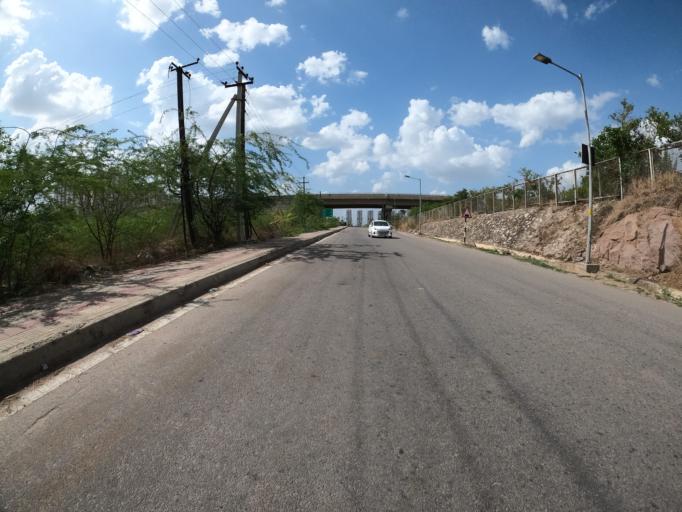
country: IN
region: Telangana
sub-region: Hyderabad
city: Hyderabad
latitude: 17.3852
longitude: 78.3506
